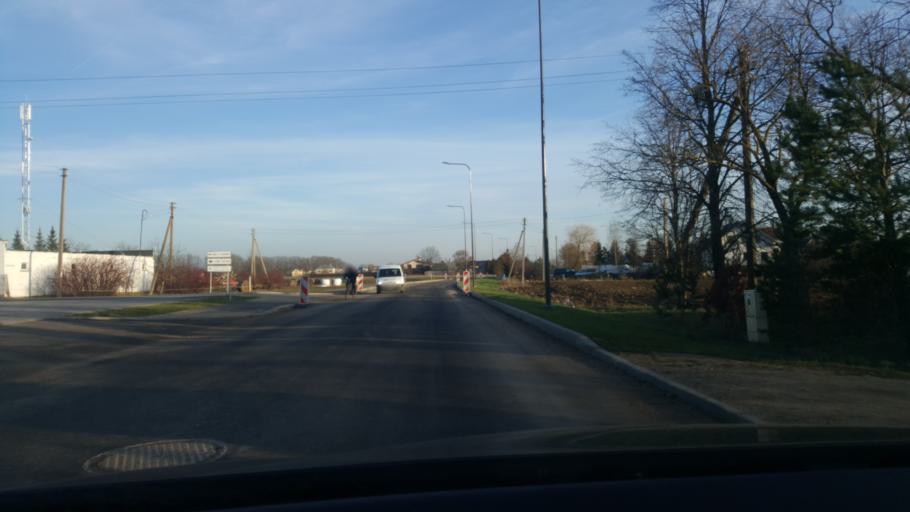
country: LT
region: Kauno apskritis
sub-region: Kauno rajonas
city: Mastaiciai
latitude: 54.8539
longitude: 23.8482
